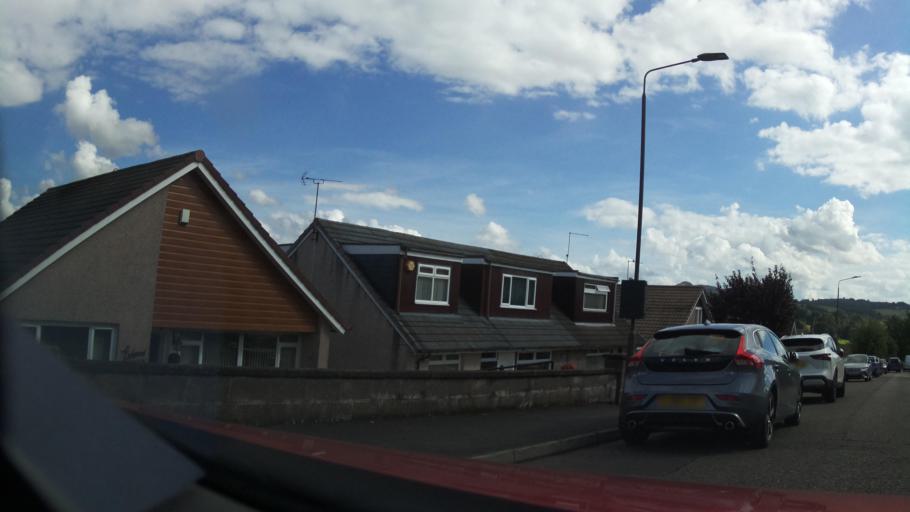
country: GB
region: Scotland
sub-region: Stirling
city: Dunblane
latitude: 56.1835
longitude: -3.9711
